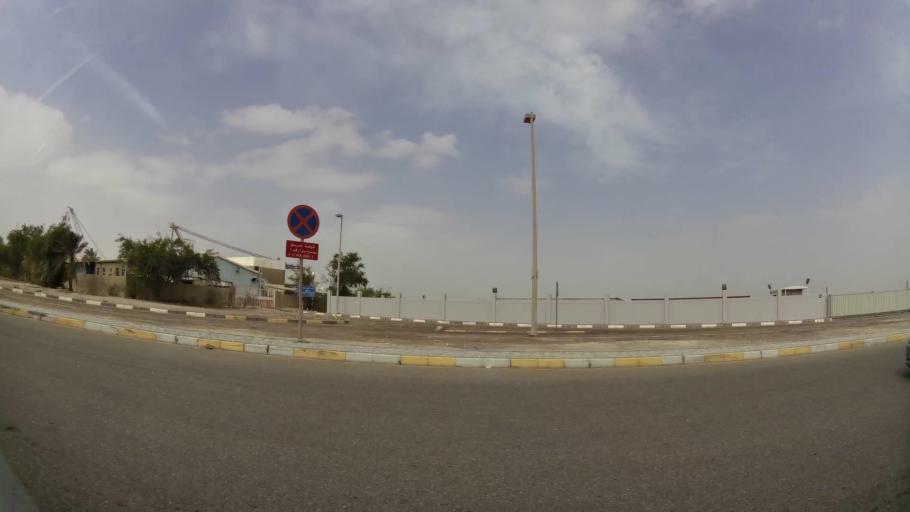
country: AE
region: Abu Dhabi
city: Abu Dhabi
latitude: 24.3814
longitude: 54.4808
